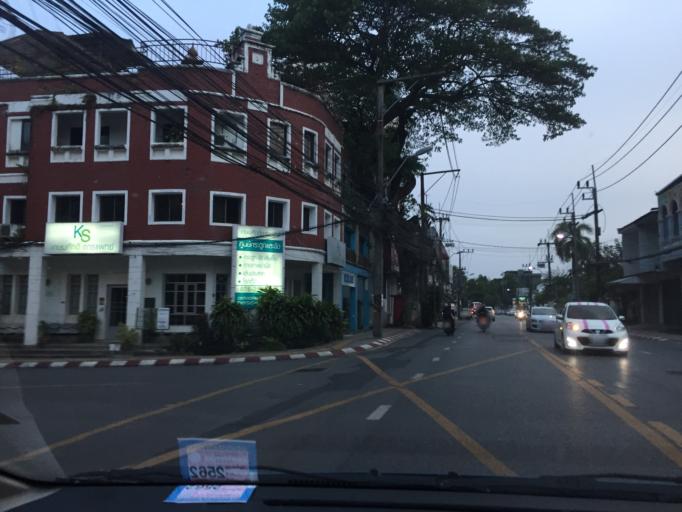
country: TH
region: Phuket
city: Wichit
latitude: 7.8918
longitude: 98.3859
